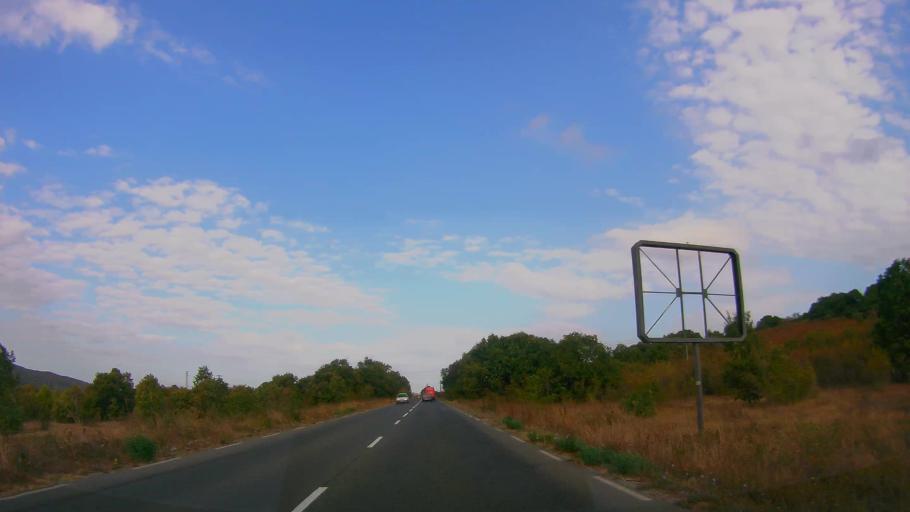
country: BG
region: Burgas
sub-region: Obshtina Sozopol
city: Sozopol
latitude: 42.3673
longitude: 27.6888
